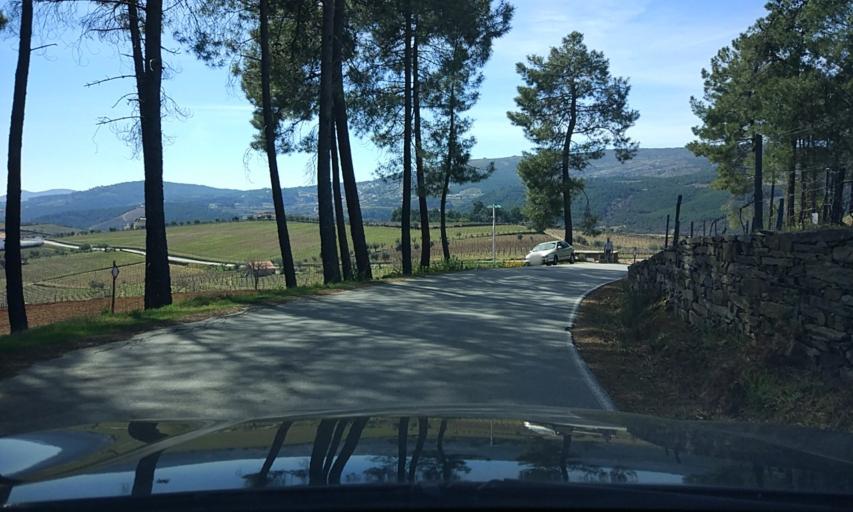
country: PT
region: Vila Real
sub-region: Sabrosa
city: Sabrosa
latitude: 41.3165
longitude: -7.5594
